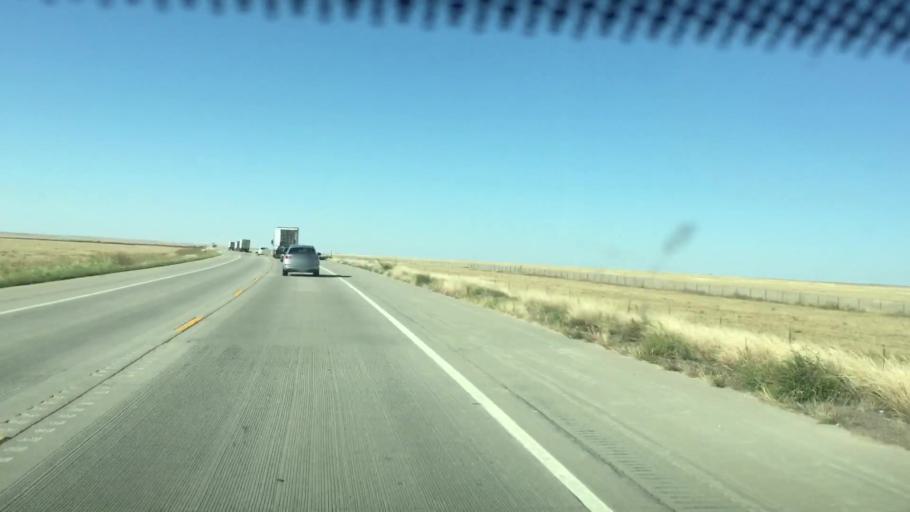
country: US
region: Colorado
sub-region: Kiowa County
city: Eads
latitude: 38.3553
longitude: -102.7163
